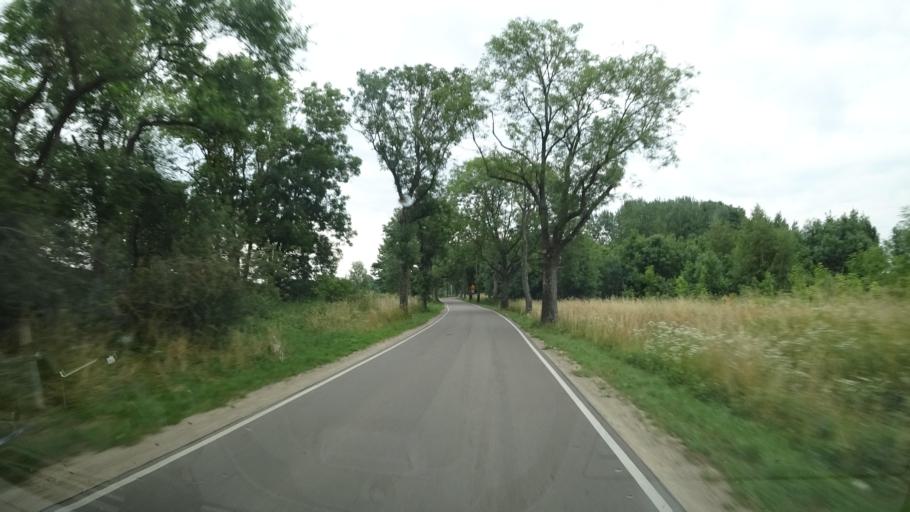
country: PL
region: Warmian-Masurian Voivodeship
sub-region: Powiat gizycki
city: Ryn
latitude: 53.8766
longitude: 21.5880
